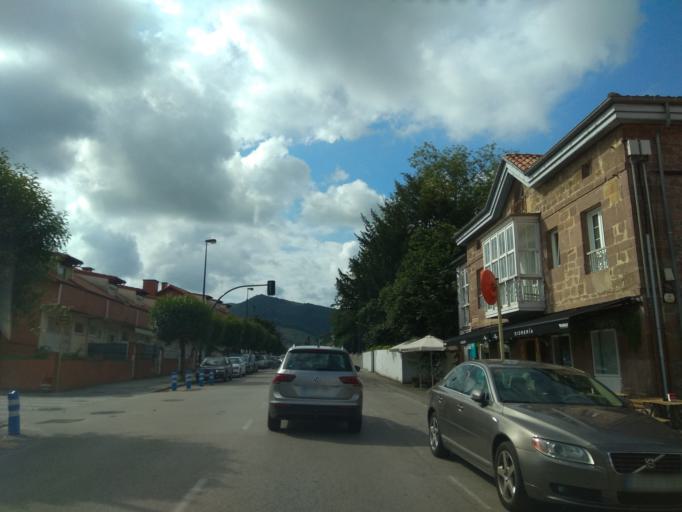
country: ES
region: Cantabria
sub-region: Provincia de Cantabria
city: Torrelavega
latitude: 43.3347
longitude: -4.0444
